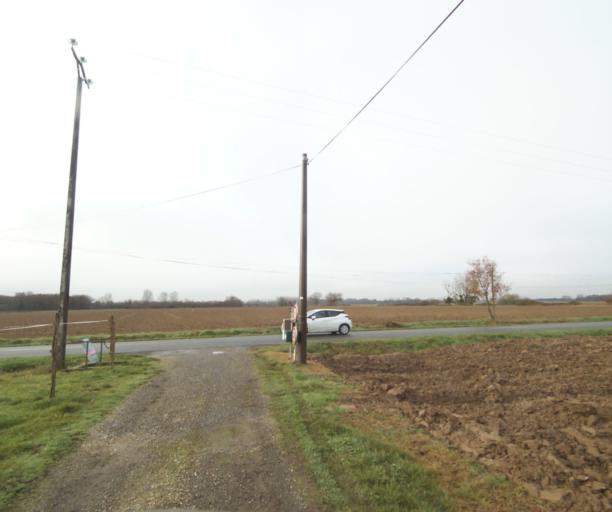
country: FR
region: Midi-Pyrenees
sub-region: Departement de la Haute-Garonne
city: Villemur-sur-Tarn
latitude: 43.8861
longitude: 1.4787
